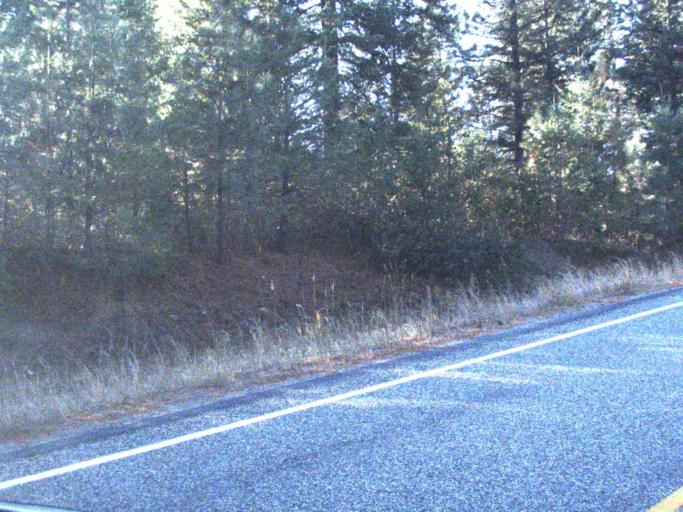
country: CA
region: British Columbia
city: Rossland
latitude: 48.9515
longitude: -117.7929
